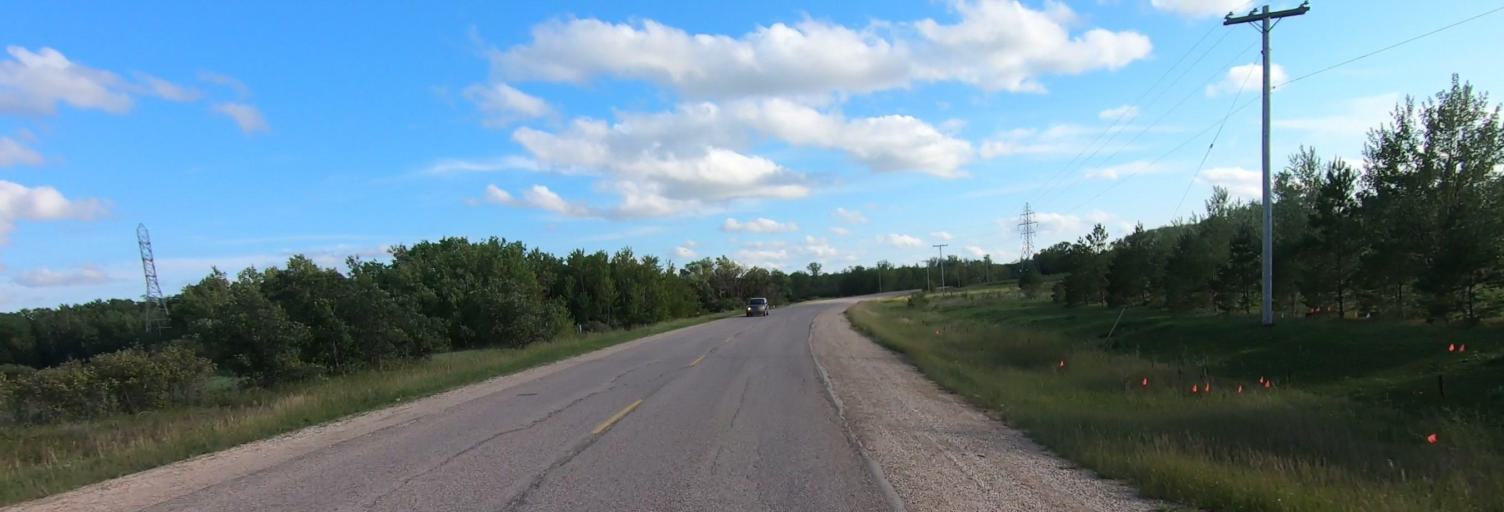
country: CA
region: Manitoba
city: Selkirk
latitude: 50.2031
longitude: -96.8389
